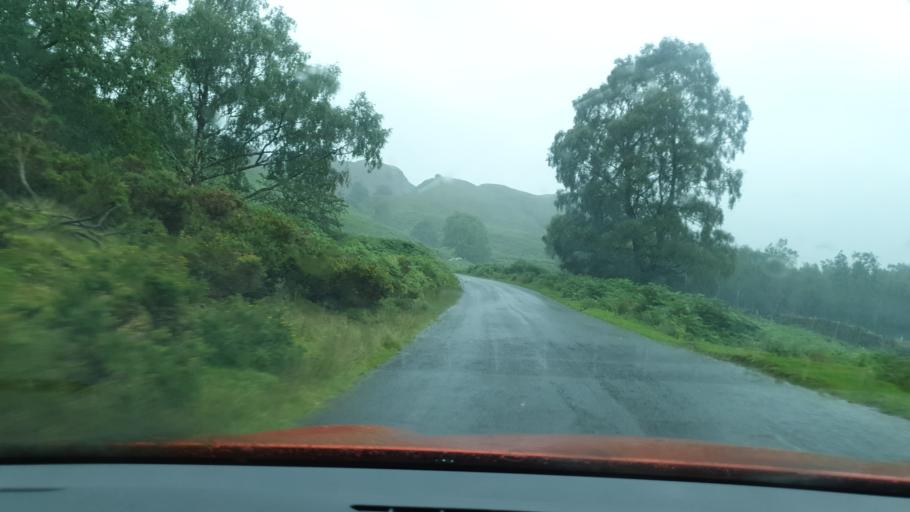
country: GB
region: England
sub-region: Cumbria
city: Millom
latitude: 54.3129
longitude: -3.2297
